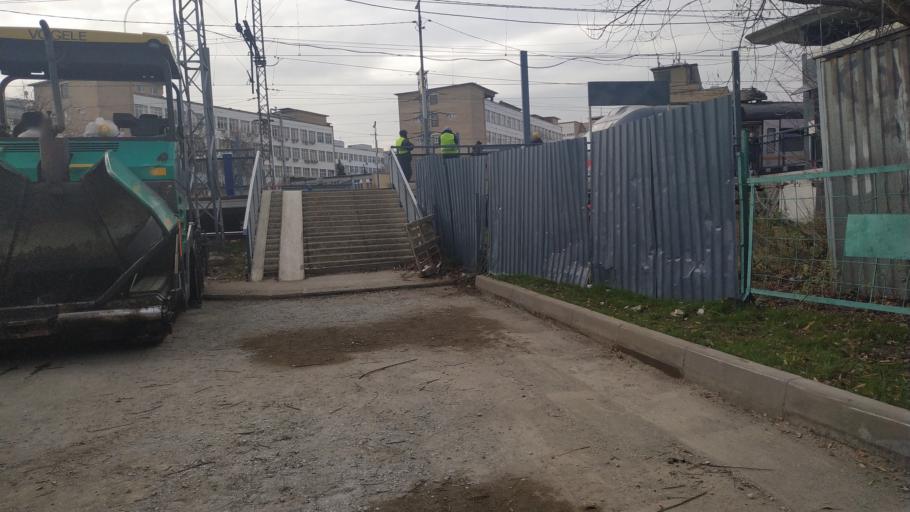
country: RU
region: Moscow
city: Sokol
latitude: 55.8054
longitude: 37.5552
